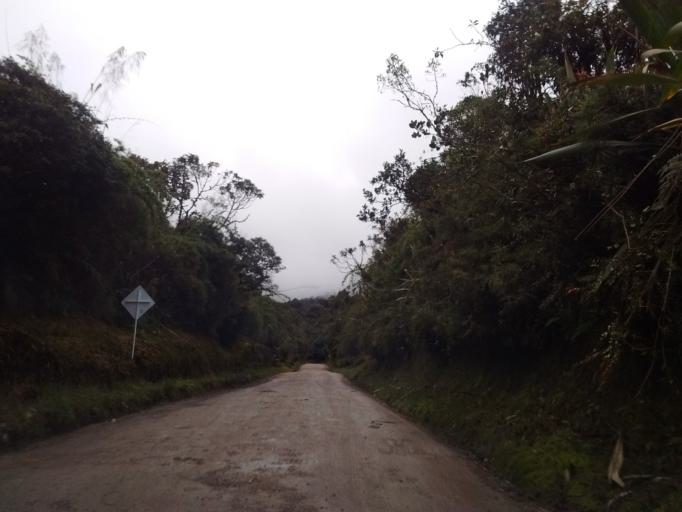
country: CO
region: Huila
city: Isnos
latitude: 2.1329
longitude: -76.3801
